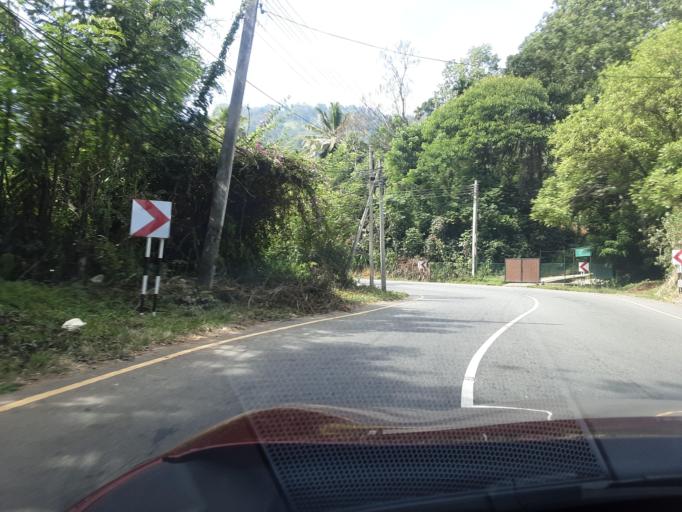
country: LK
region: Uva
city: Badulla
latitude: 6.9680
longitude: 81.0879
